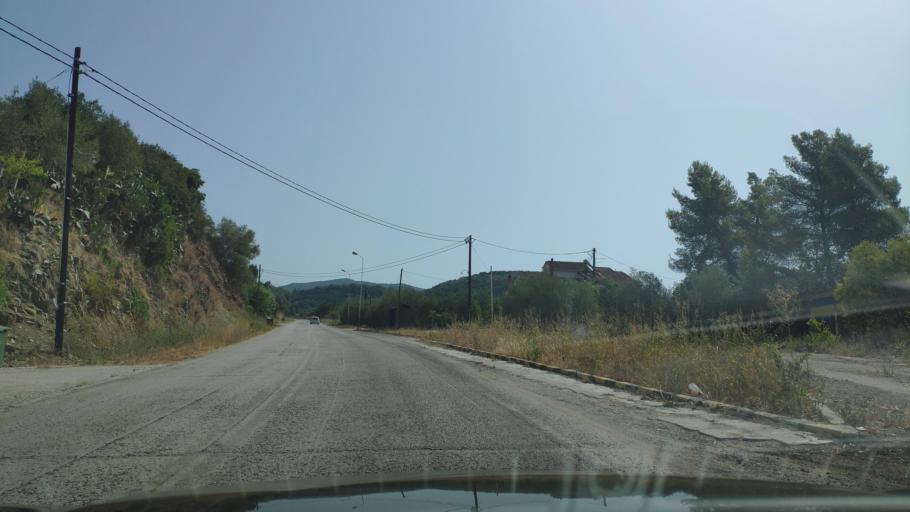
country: GR
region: Epirus
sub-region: Nomos Artas
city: Peta
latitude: 39.1574
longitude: 21.0286
